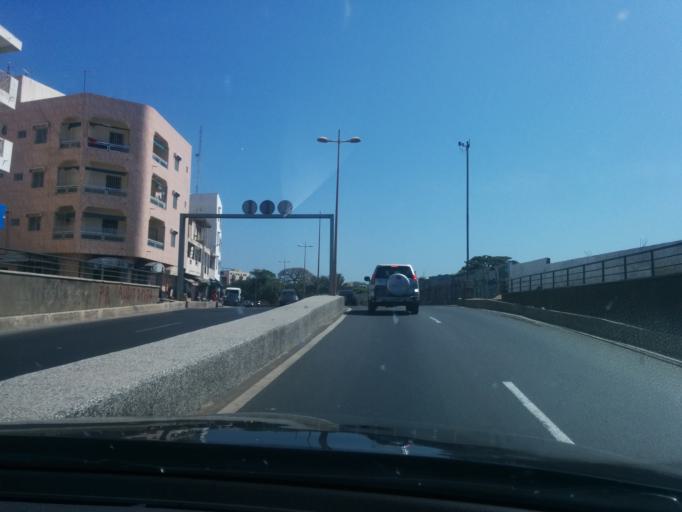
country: SN
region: Dakar
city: Dakar
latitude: 14.6767
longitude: -17.4568
